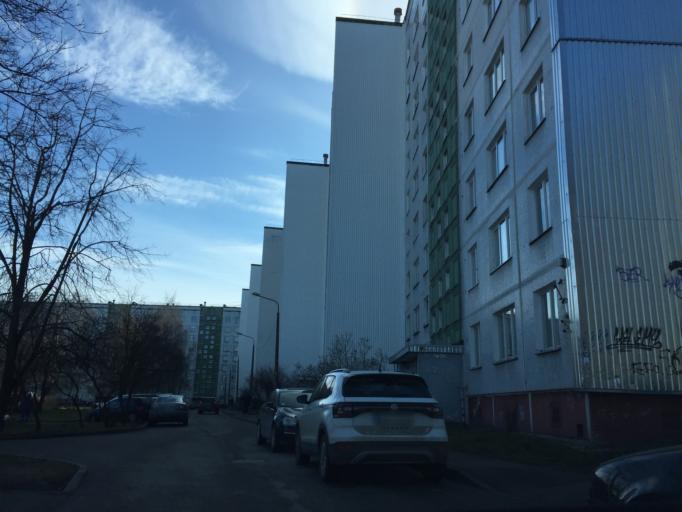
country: LV
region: Stopini
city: Ulbroka
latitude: 56.9354
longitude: 24.1982
